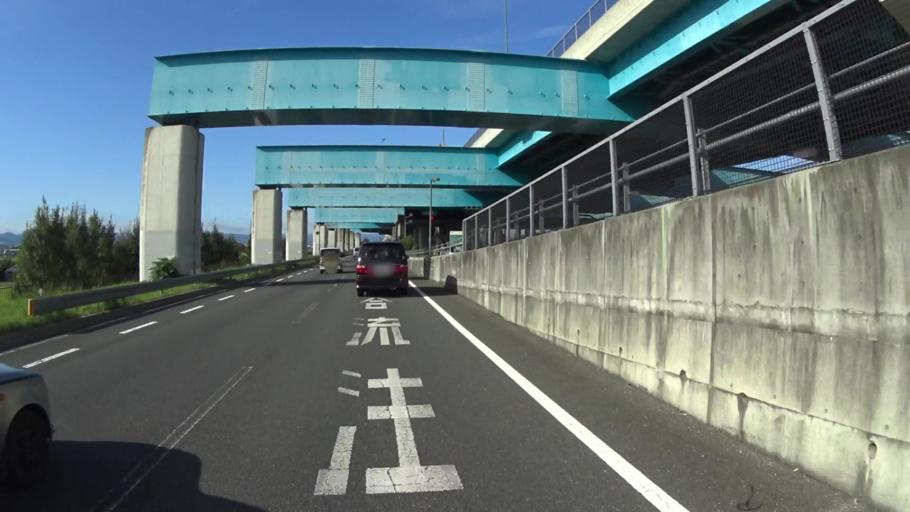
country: JP
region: Kyoto
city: Uji
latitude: 34.9074
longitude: 135.7499
